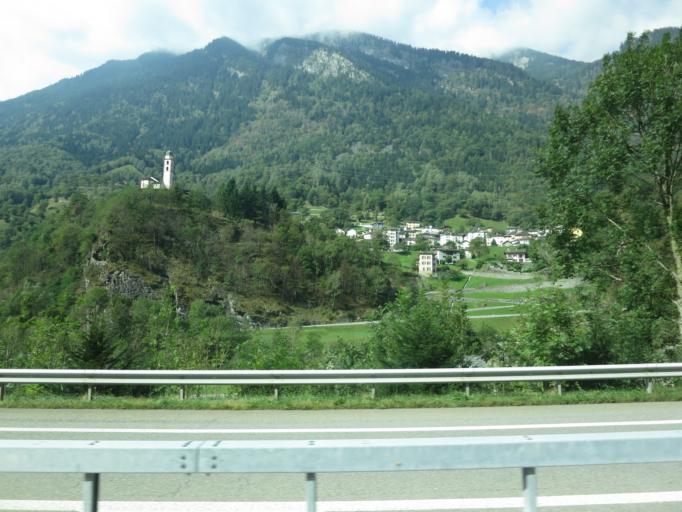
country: CH
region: Grisons
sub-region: Moesa District
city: Mesocco
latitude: 46.3645
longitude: 9.2271
